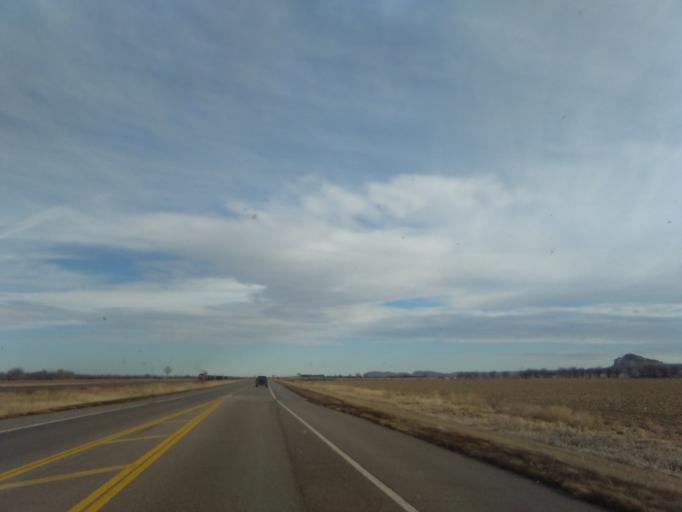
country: US
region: Nebraska
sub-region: Scotts Bluff County
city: Gering
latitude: 41.7823
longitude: -103.5133
